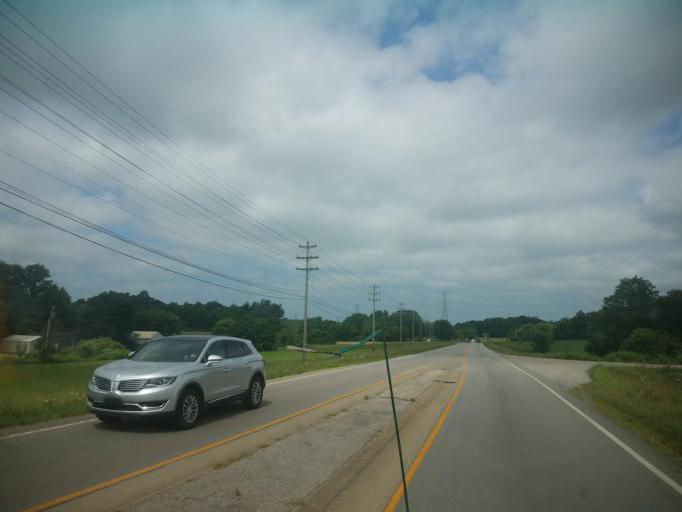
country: US
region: Kentucky
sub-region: Metcalfe County
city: Edmonton
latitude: 36.8785
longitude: -85.6681
